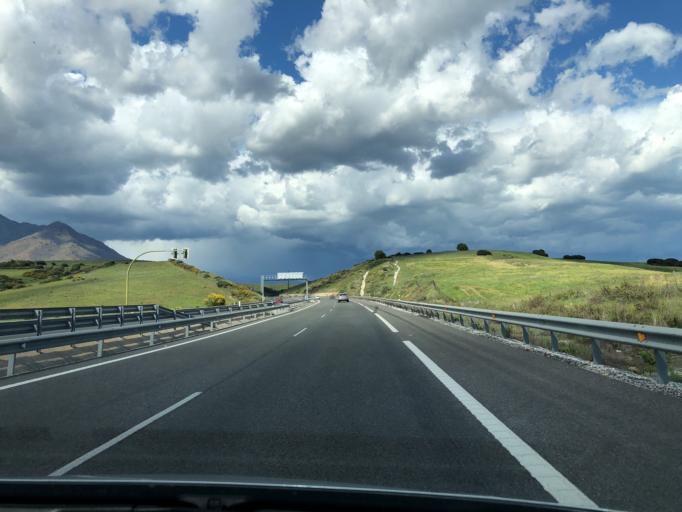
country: ES
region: Andalusia
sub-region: Provincia de Malaga
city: Manilva
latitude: 36.4082
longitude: -5.2270
